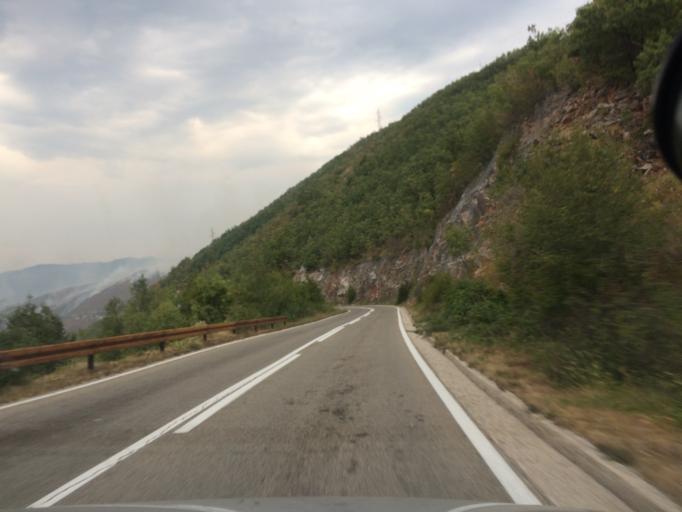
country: ME
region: Opstina Niksic
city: Niksic
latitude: 42.8862
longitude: 18.9537
